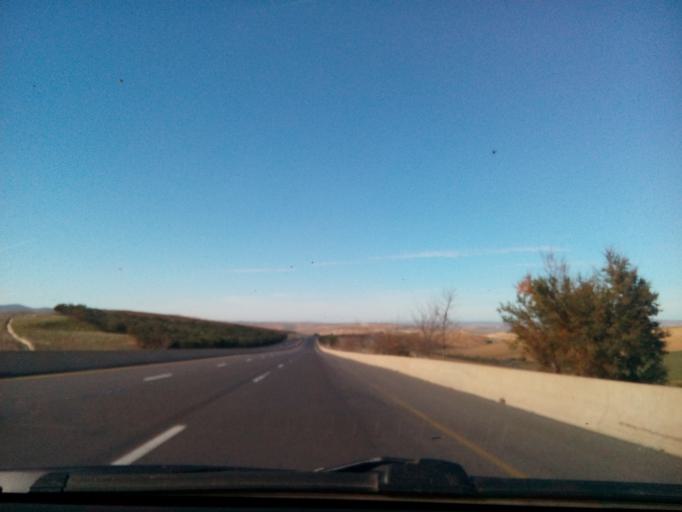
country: DZ
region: Tlemcen
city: Ouled Mimoun
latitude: 35.0303
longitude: -1.0106
